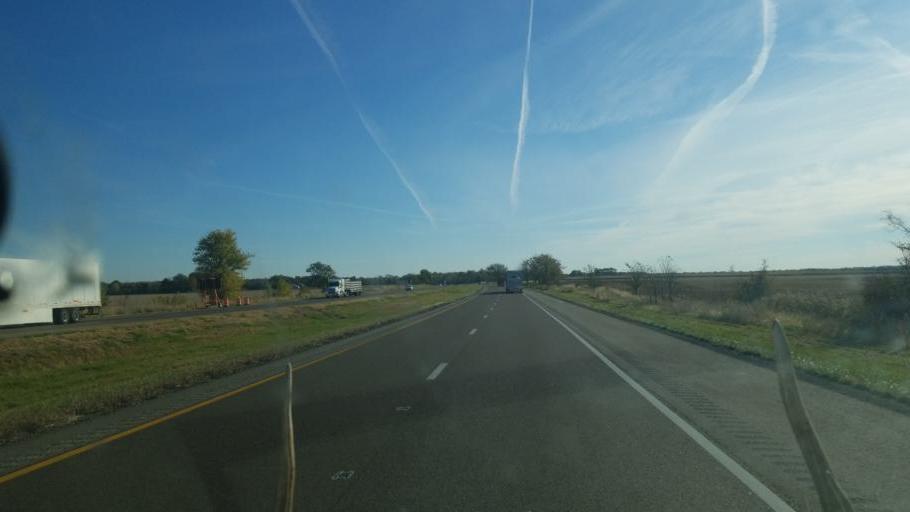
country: US
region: Illinois
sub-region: Madison County
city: Troy
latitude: 38.7553
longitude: -89.8607
